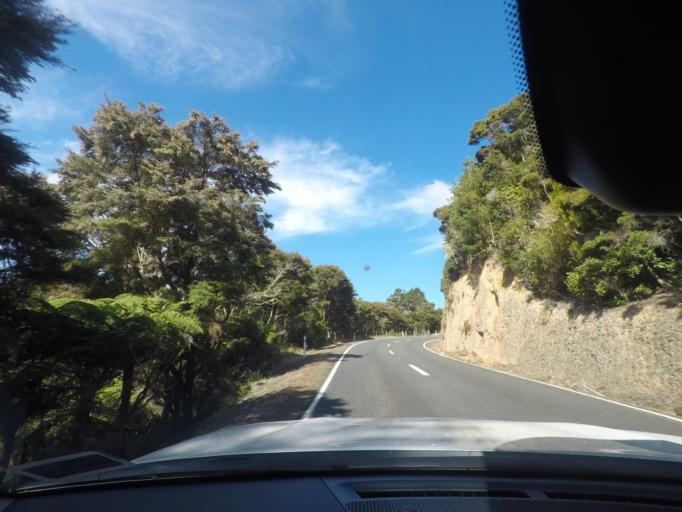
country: NZ
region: Northland
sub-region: Whangarei
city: Ngunguru
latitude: -35.6716
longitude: 174.4611
